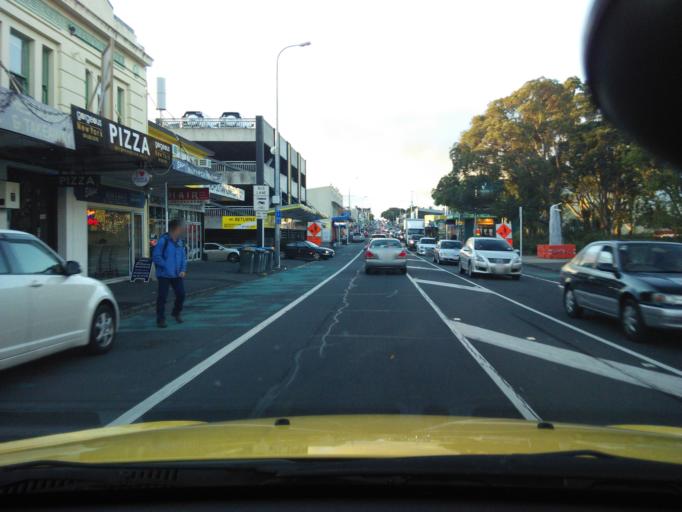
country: NZ
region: Auckland
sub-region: Auckland
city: Auckland
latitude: -36.8789
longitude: 174.7501
